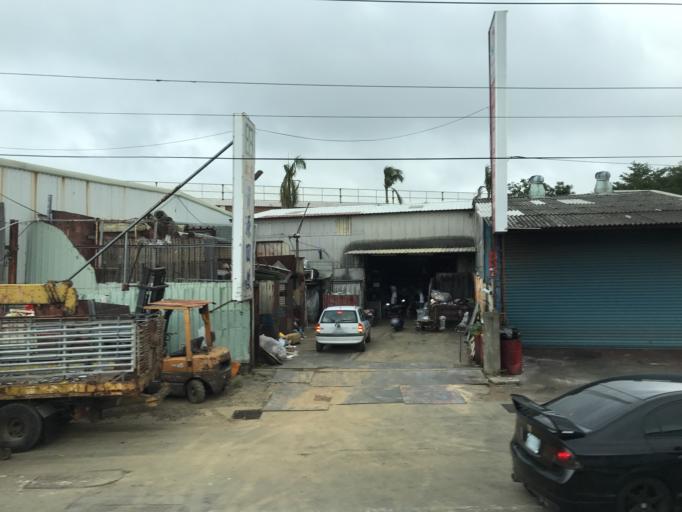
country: TW
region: Taiwan
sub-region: Hsinchu
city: Hsinchu
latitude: 24.8174
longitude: 120.9563
